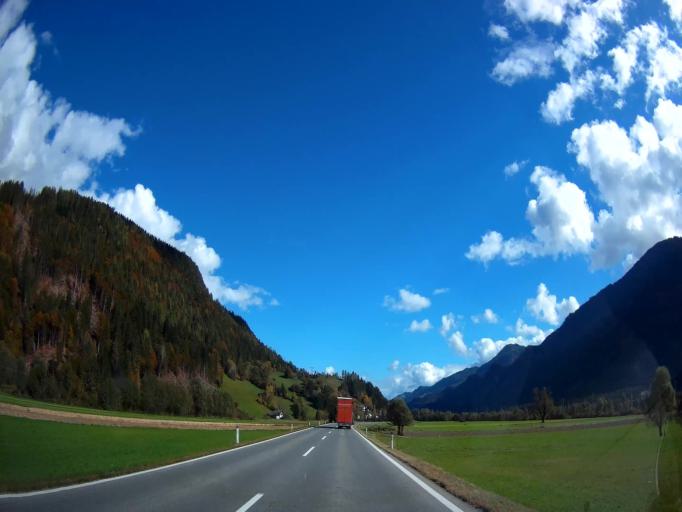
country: AT
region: Carinthia
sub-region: Politischer Bezirk Spittal an der Drau
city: Dellach im Drautal
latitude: 46.7404
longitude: 13.0496
